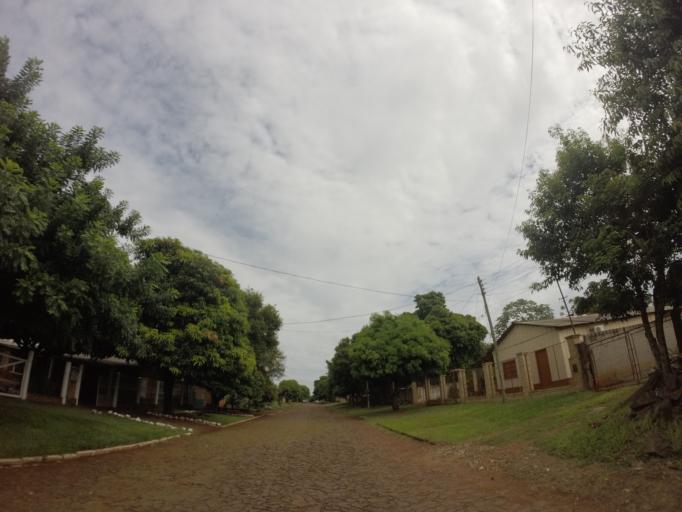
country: PY
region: Alto Parana
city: Ciudad del Este
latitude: -25.4062
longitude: -54.6476
